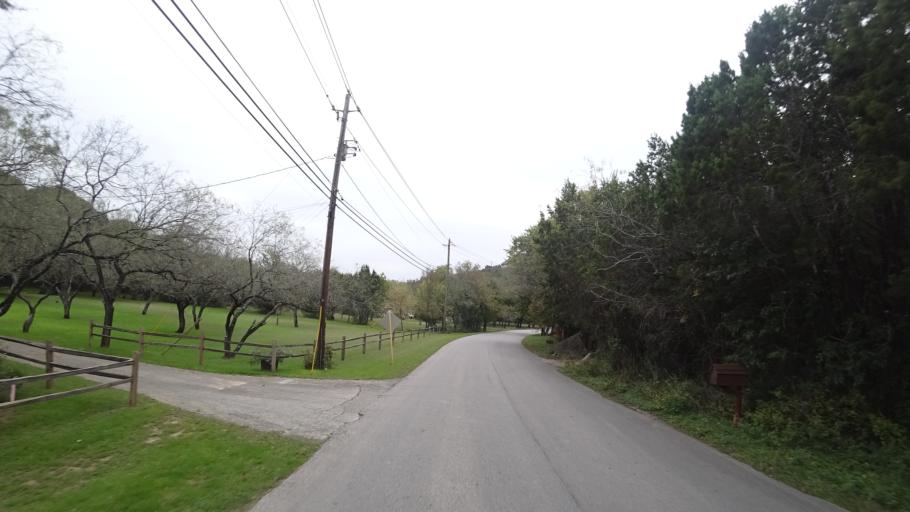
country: US
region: Texas
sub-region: Travis County
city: Hudson Bend
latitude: 30.3792
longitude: -97.9202
